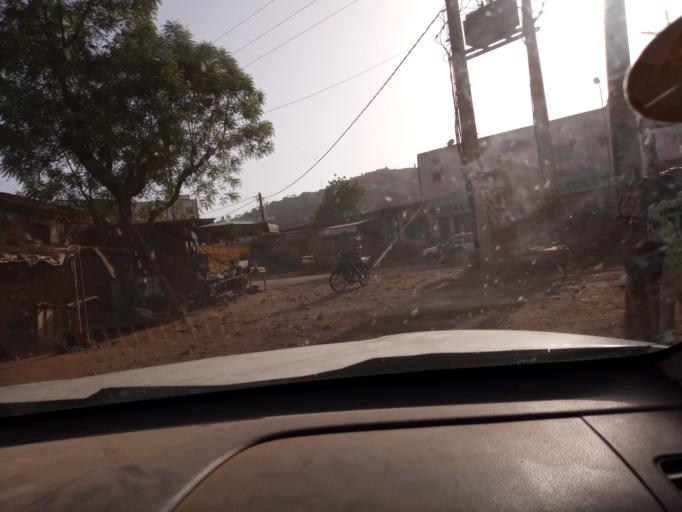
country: ML
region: Bamako
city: Bamako
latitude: 12.6699
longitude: -7.9774
